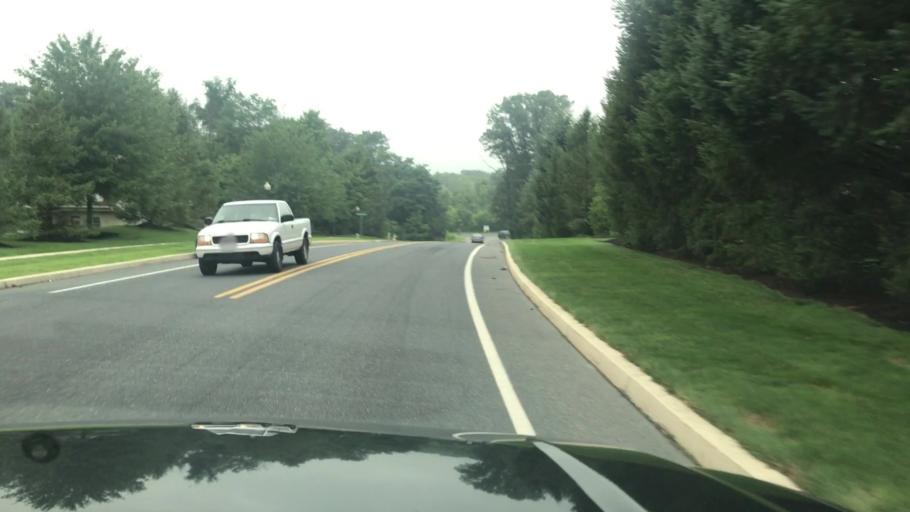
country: US
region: Pennsylvania
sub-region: Cumberland County
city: Enola
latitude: 40.2784
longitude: -76.9769
